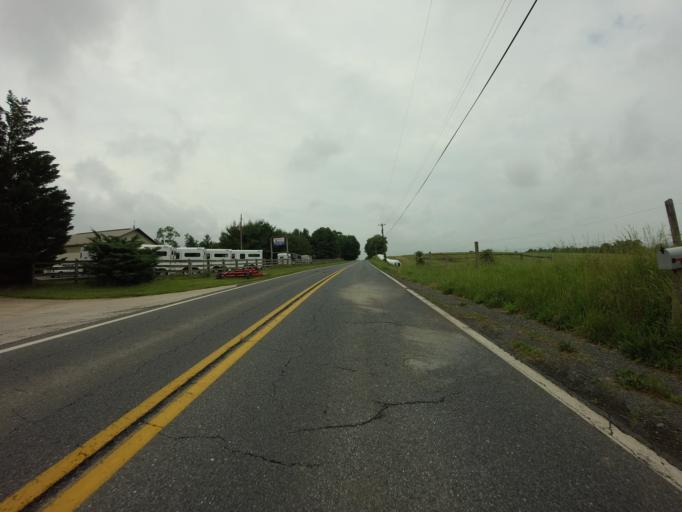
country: US
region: Maryland
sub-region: Frederick County
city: Jefferson
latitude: 39.3466
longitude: -77.5362
